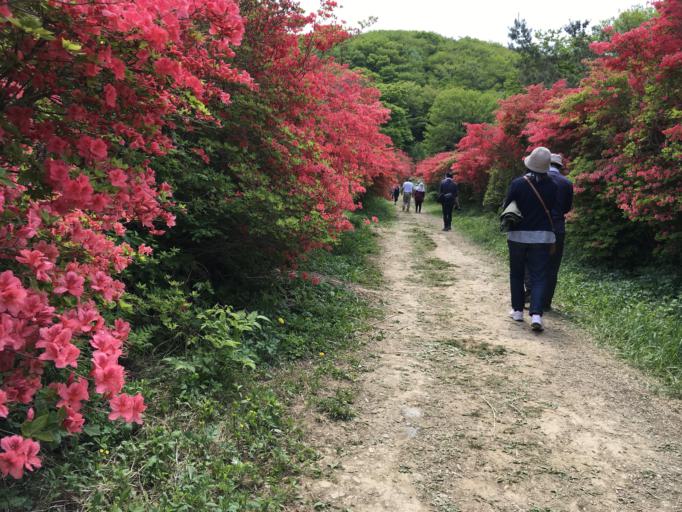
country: JP
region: Iwate
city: Ofunato
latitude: 38.8502
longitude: 141.4713
